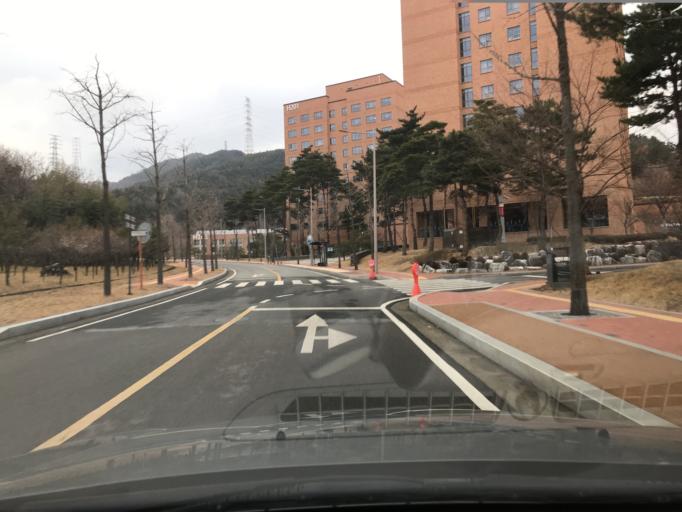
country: KR
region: Daegu
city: Hwawon
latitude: 35.7026
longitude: 128.4611
